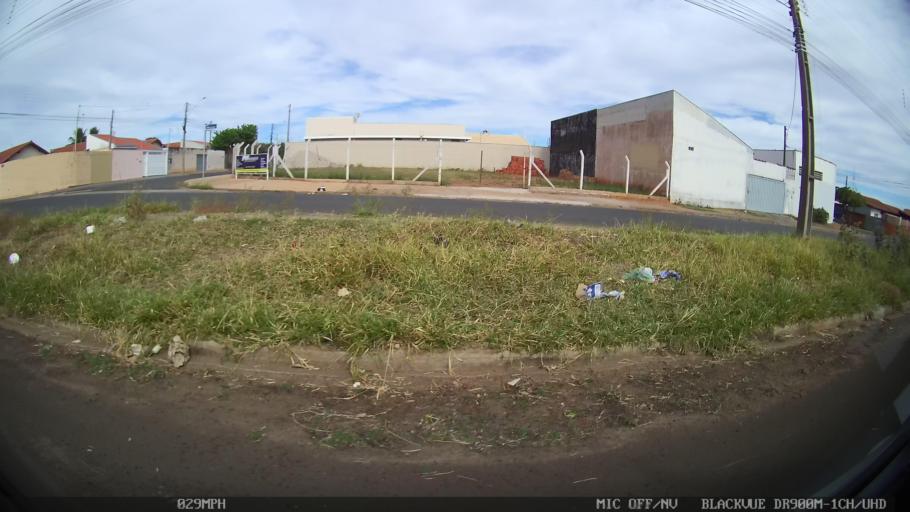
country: BR
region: Sao Paulo
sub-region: Catanduva
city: Catanduva
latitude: -21.1632
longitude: -48.9668
